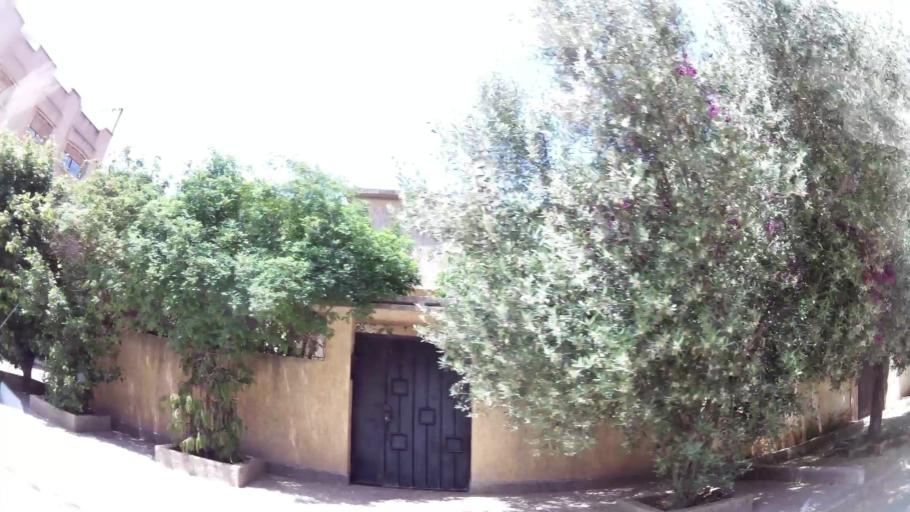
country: MA
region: Rabat-Sale-Zemmour-Zaer
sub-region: Khemisset
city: Khemisset
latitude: 33.8257
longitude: -6.0832
